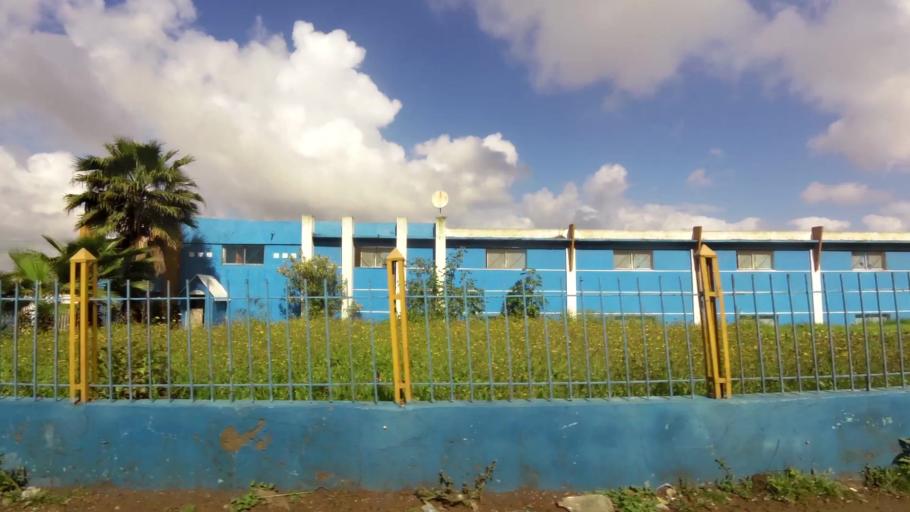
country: MA
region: Grand Casablanca
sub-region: Nouaceur
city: Bouskoura
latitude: 33.5338
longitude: -7.6853
